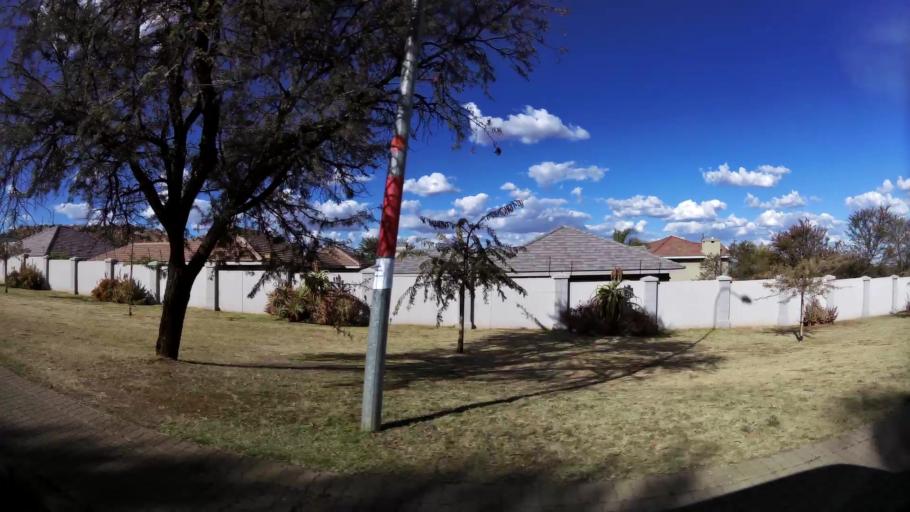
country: ZA
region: North-West
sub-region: Dr Kenneth Kaunda District Municipality
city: Klerksdorp
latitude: -26.8227
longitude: 26.6785
